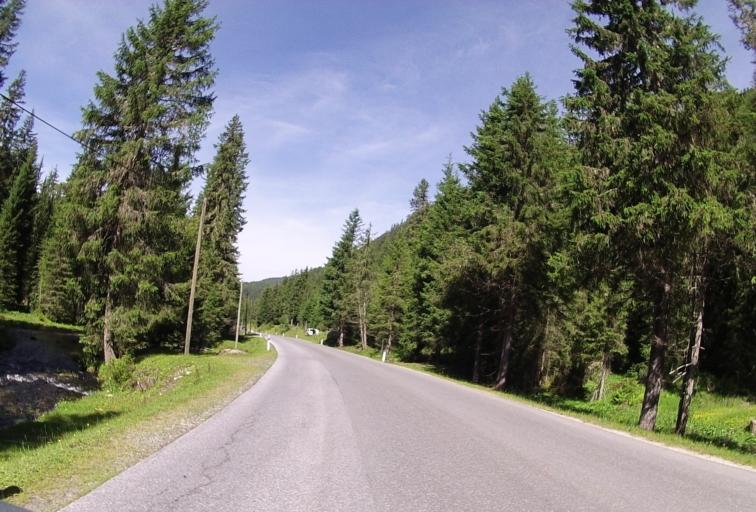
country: AT
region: Tyrol
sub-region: Politischer Bezirk Imst
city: Silz
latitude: 47.2299
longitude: 10.9495
